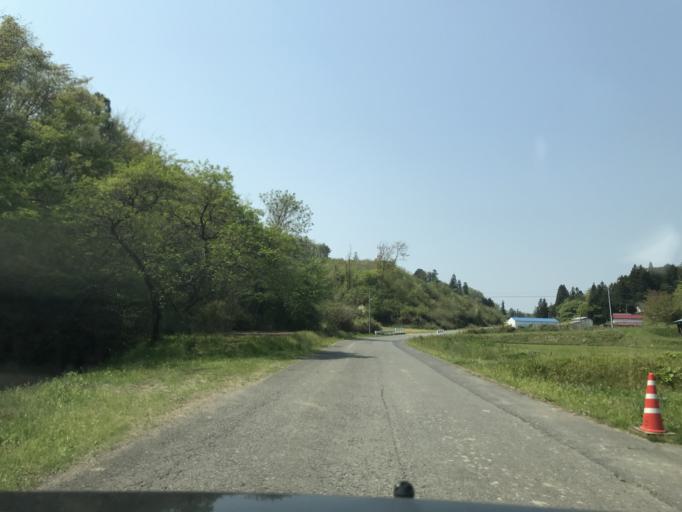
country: JP
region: Iwate
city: Ichinoseki
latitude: 38.8920
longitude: 141.0749
